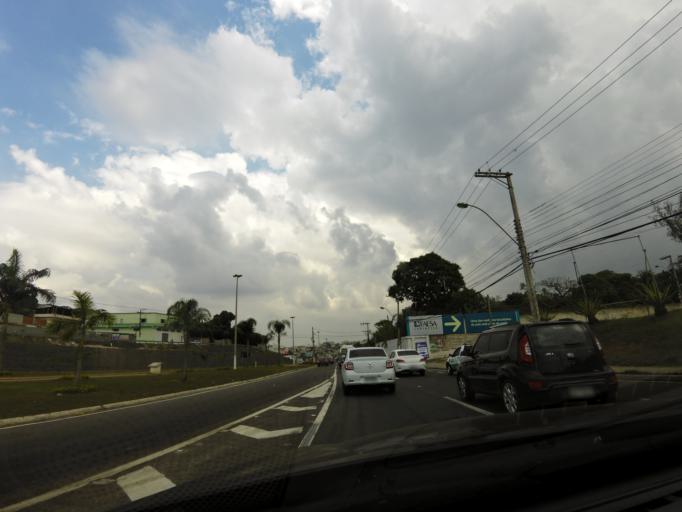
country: BR
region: Espirito Santo
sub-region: Vitoria
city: Vitoria
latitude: -20.3354
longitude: -40.3769
